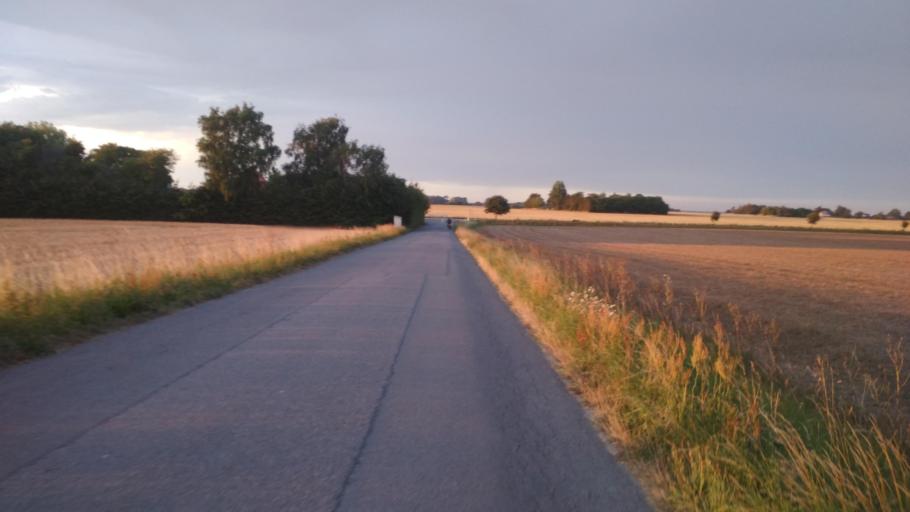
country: DK
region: Capital Region
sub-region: Bornholm Kommune
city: Akirkeby
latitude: 55.0333
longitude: 14.9151
